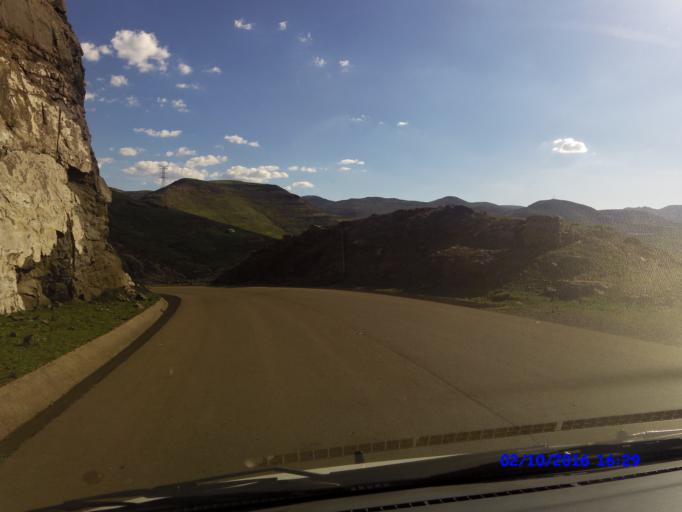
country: LS
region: Maseru
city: Nako
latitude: -29.4749
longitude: 28.0834
